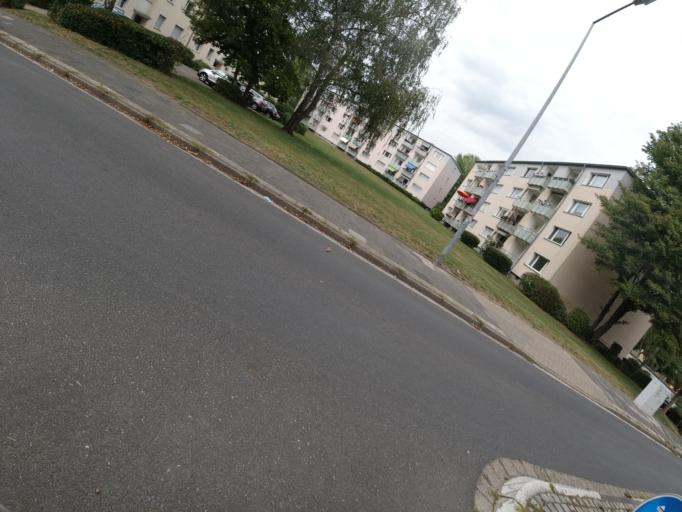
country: DE
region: North Rhine-Westphalia
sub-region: Regierungsbezirk Dusseldorf
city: Moers
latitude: 51.4426
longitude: 6.6328
